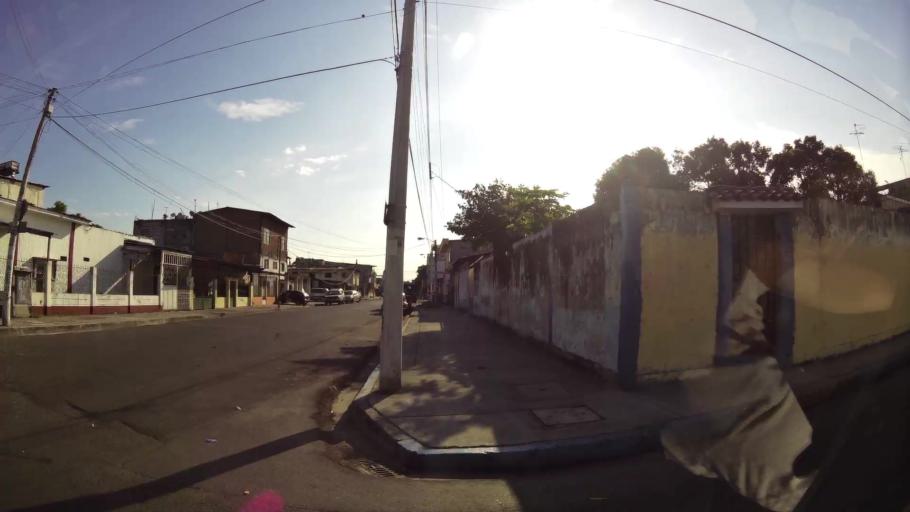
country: EC
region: Guayas
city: Guayaquil
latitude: -2.2172
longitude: -79.9086
